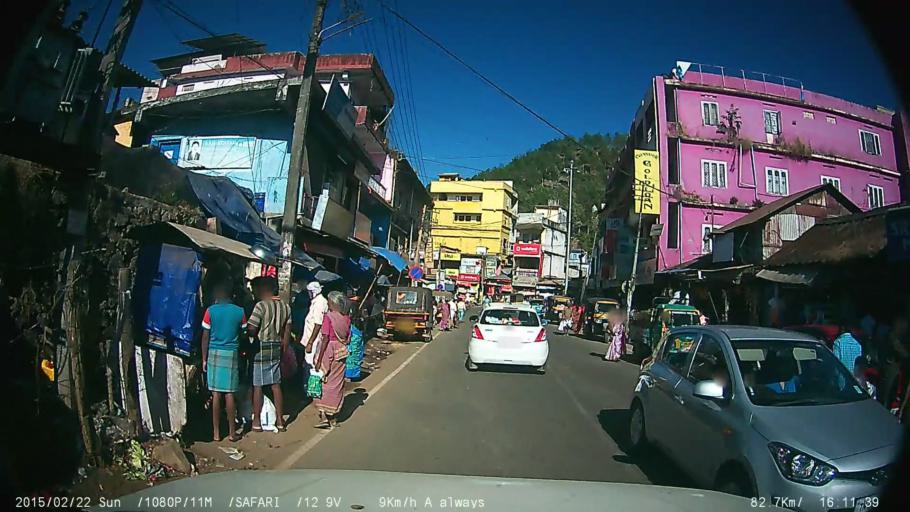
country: IN
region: Tamil Nadu
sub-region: Theni
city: Gudalur
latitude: 9.5728
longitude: 77.0918
